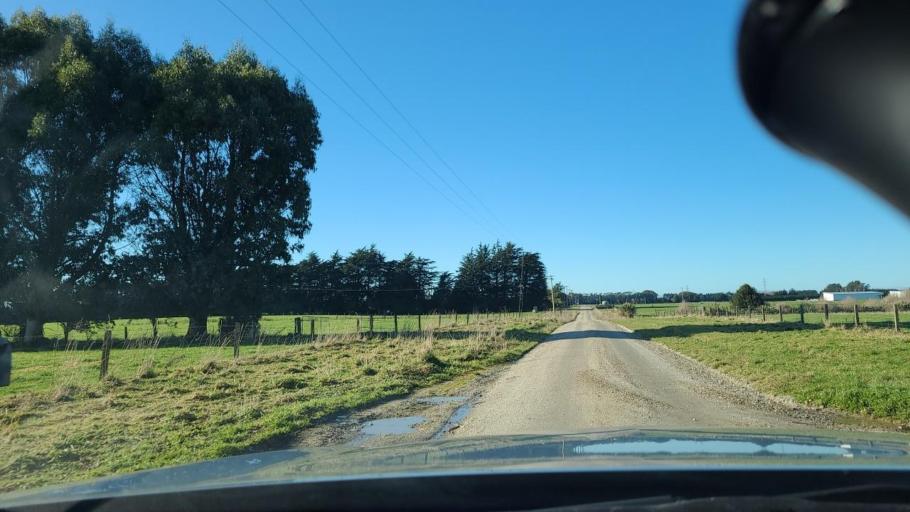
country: NZ
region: Southland
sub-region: Invercargill City
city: Invercargill
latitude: -46.2848
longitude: 168.6086
